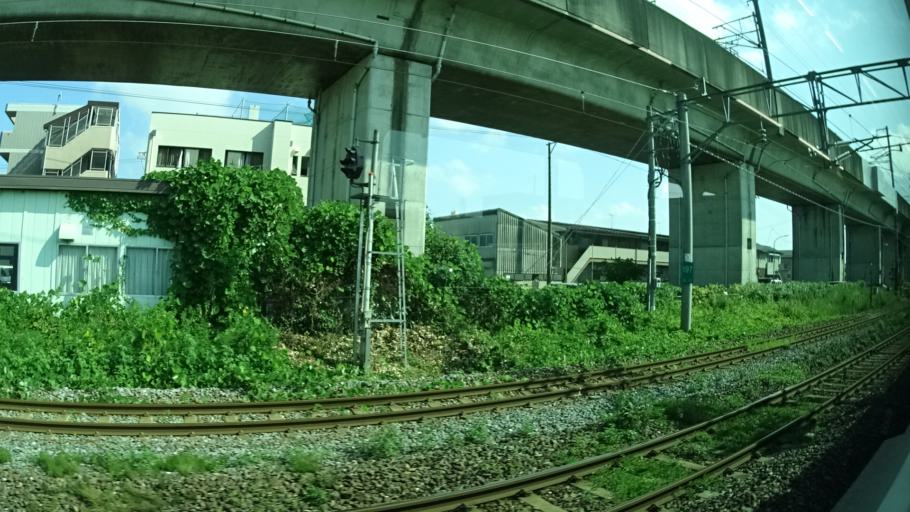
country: JP
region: Miyagi
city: Sendai-shi
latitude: 38.2755
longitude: 140.9185
